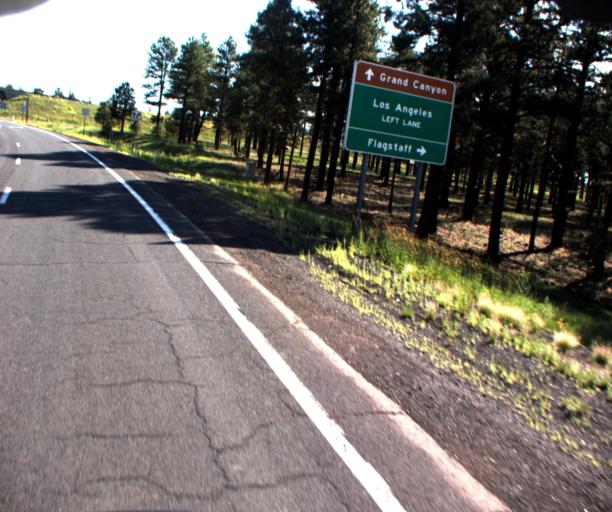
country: US
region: Arizona
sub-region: Coconino County
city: Williams
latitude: 35.2587
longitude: -112.1523
